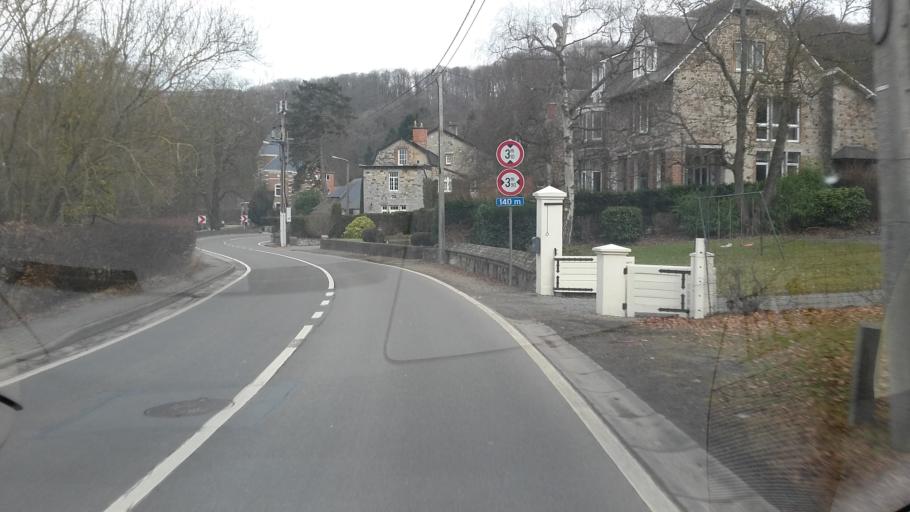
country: BE
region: Wallonia
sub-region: Province de Namur
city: Yvoir
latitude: 50.3519
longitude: 4.8782
